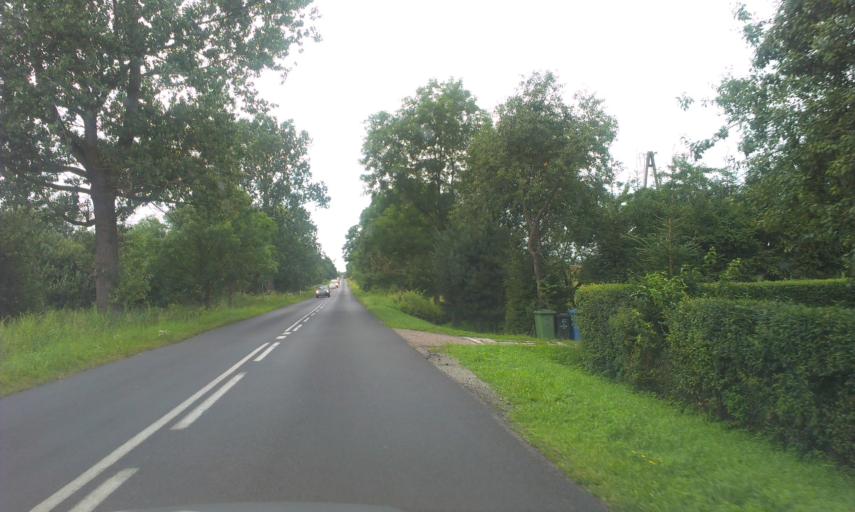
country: PL
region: West Pomeranian Voivodeship
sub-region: Powiat kolobrzeski
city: Dygowo
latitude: 54.1175
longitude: 15.7830
